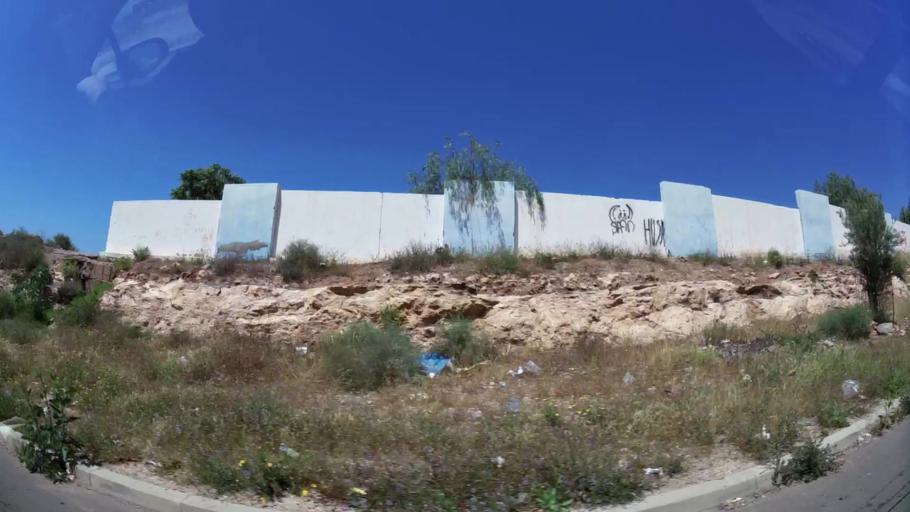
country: MA
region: Oued ed Dahab-Lagouira
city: Dakhla
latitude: 30.4338
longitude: -9.5486
